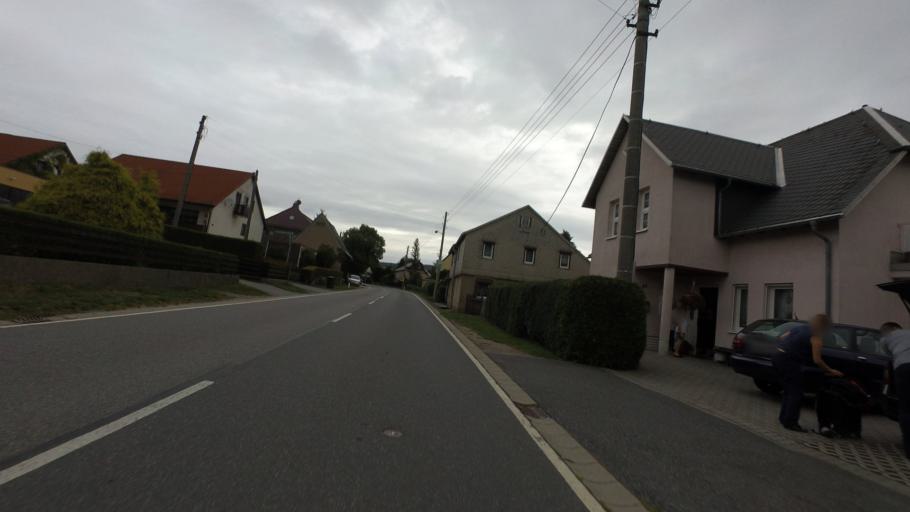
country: DE
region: Saxony
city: Berthelsdorf
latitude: 51.0545
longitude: 14.2283
